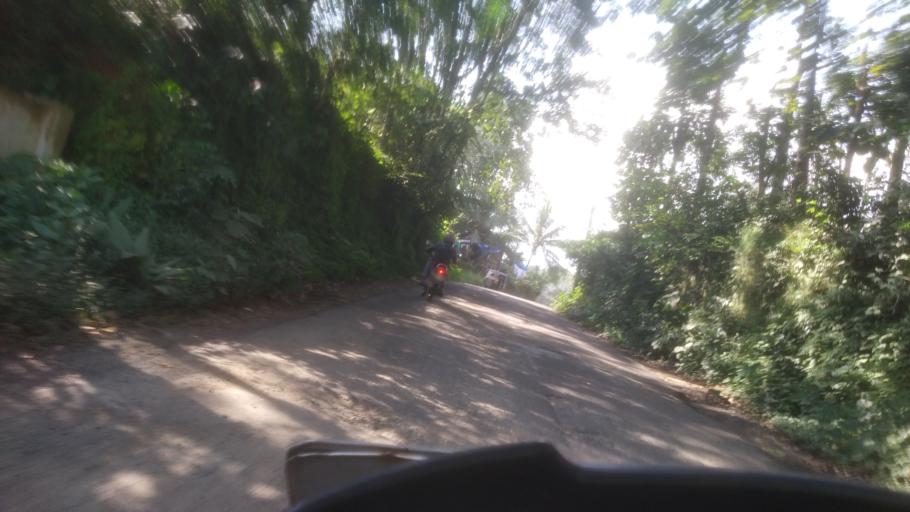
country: IN
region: Kerala
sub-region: Ernakulam
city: Kotamangalam
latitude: 10.0045
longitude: 76.6950
